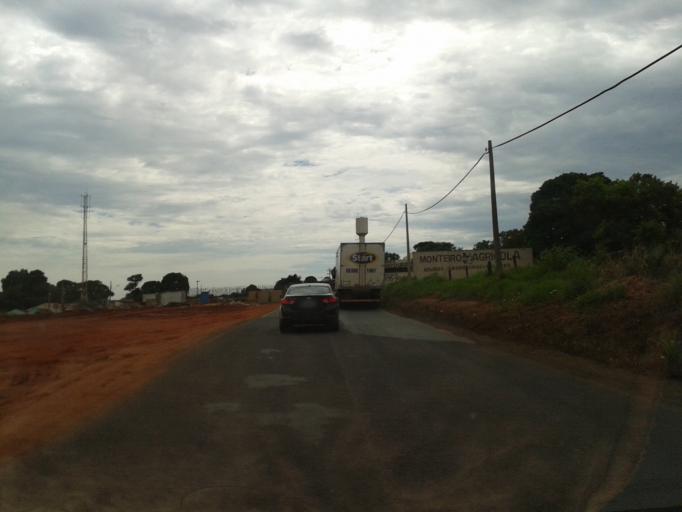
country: BR
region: Minas Gerais
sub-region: Monte Alegre De Minas
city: Monte Alegre de Minas
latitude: -18.8766
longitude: -48.8808
